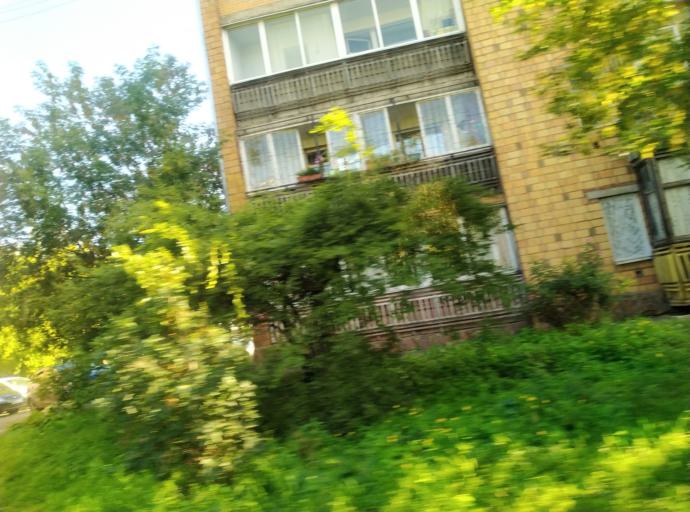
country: RU
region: Krasnoyarskiy
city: Krasnoyarsk
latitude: 55.9779
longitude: 92.8427
